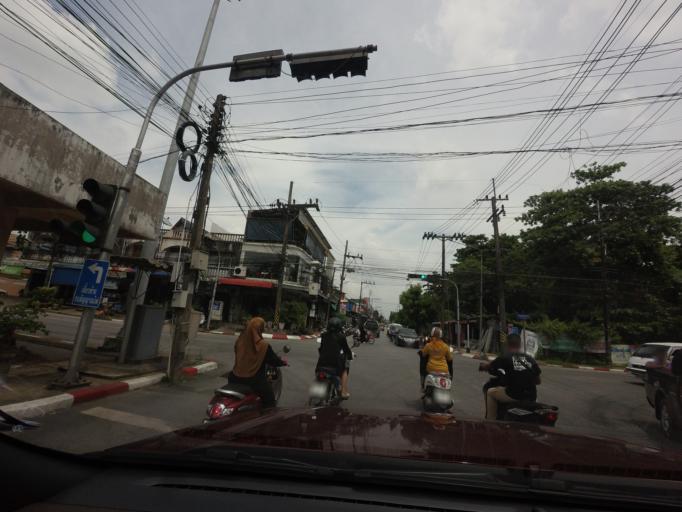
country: TH
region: Yala
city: Yala
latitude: 6.5519
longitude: 101.2956
